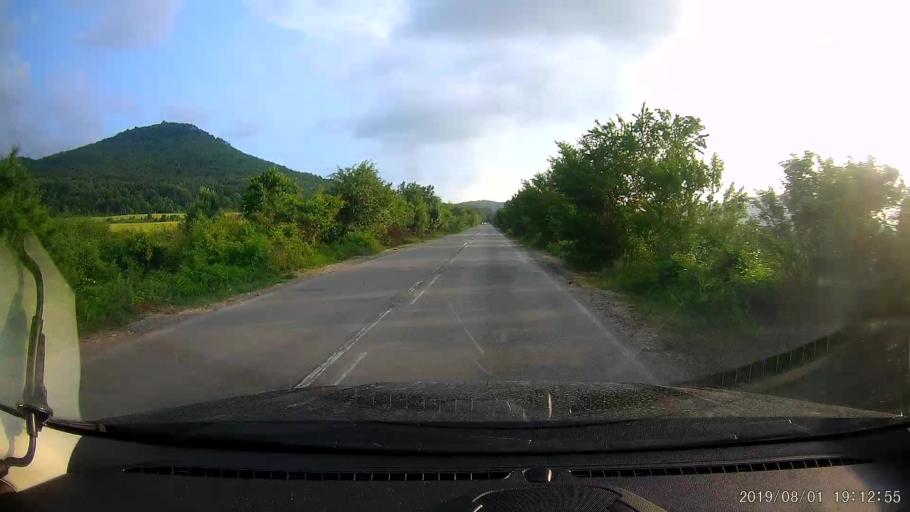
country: BG
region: Shumen
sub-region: Obshtina Smyadovo
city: Smyadovo
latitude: 42.9578
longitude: 26.9464
